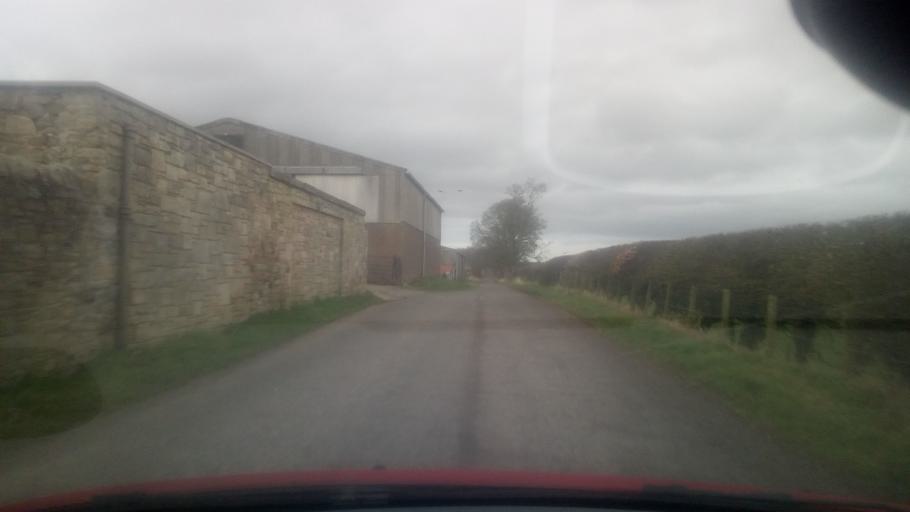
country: GB
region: Scotland
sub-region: The Scottish Borders
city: Jedburgh
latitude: 55.4595
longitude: -2.5117
